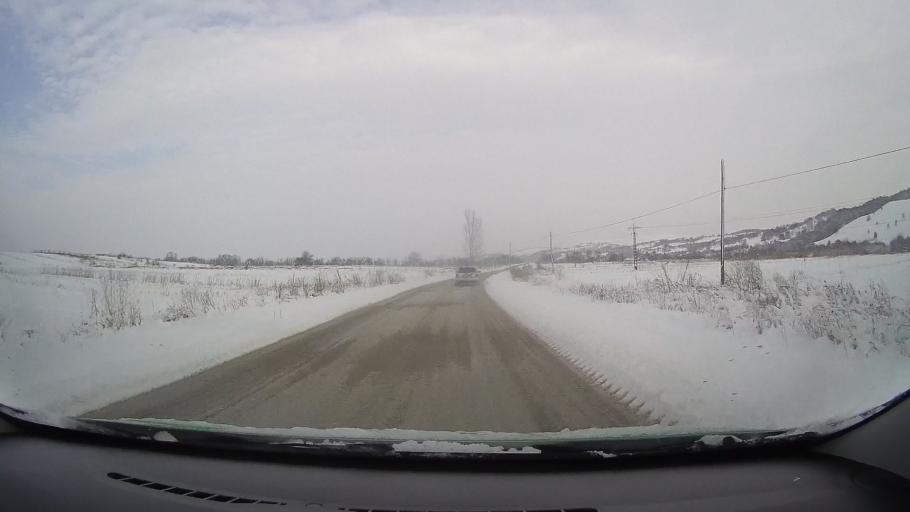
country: RO
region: Alba
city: Pianu de Sus
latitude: 45.9115
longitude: 23.4809
